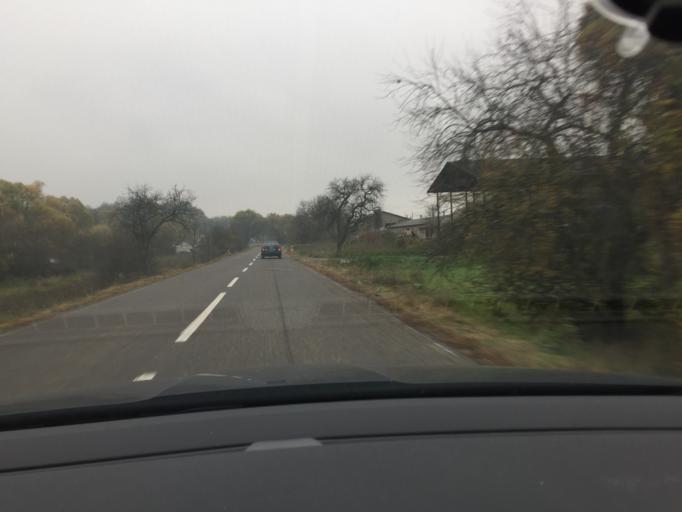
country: SK
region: Banskobystricky
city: Dudince
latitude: 48.1497
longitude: 18.9067
